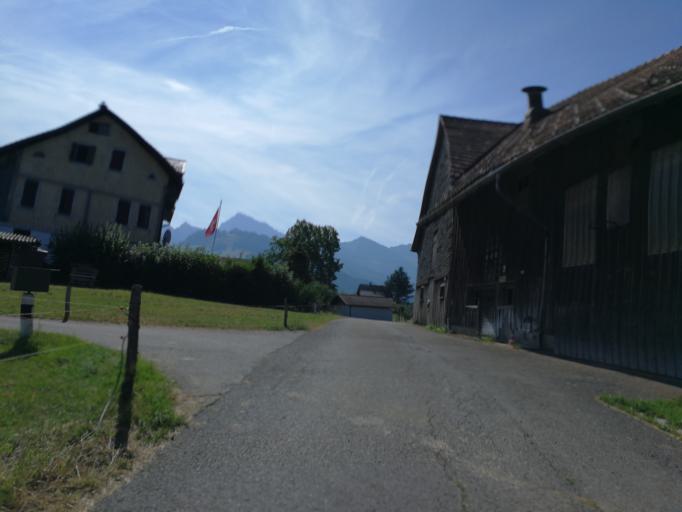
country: CH
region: Saint Gallen
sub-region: Wahlkreis See-Gaster
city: Gommiswald
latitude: 47.2281
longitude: 9.0281
